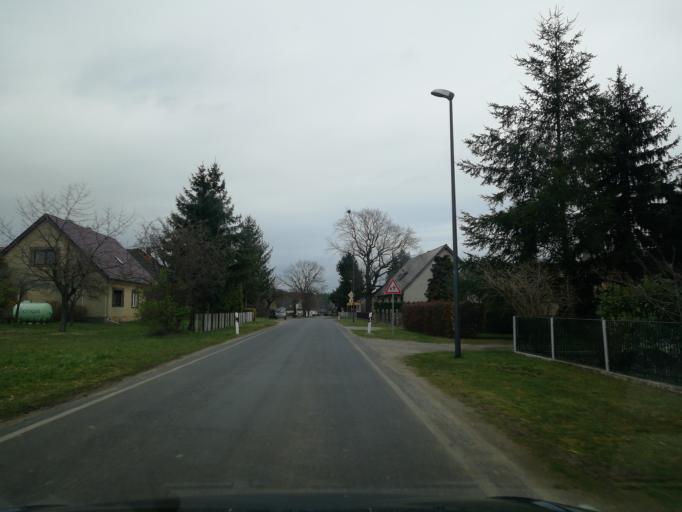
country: DE
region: Brandenburg
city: Vetschau
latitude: 51.7486
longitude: 14.0275
